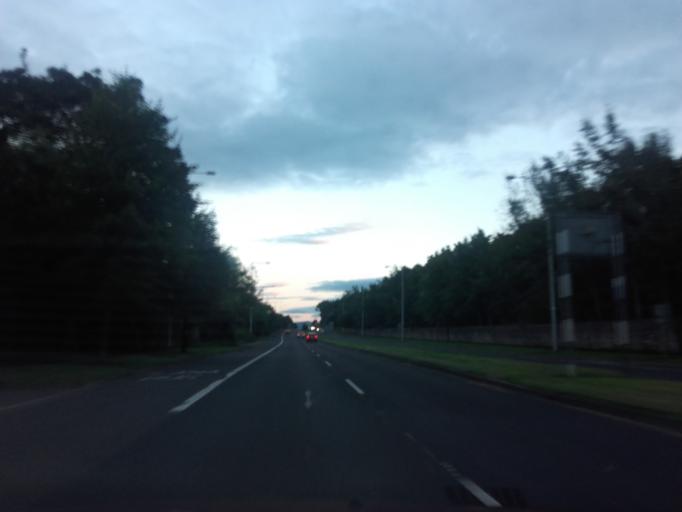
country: IE
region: Leinster
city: Clondalkin
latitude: 53.3069
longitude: -6.3833
